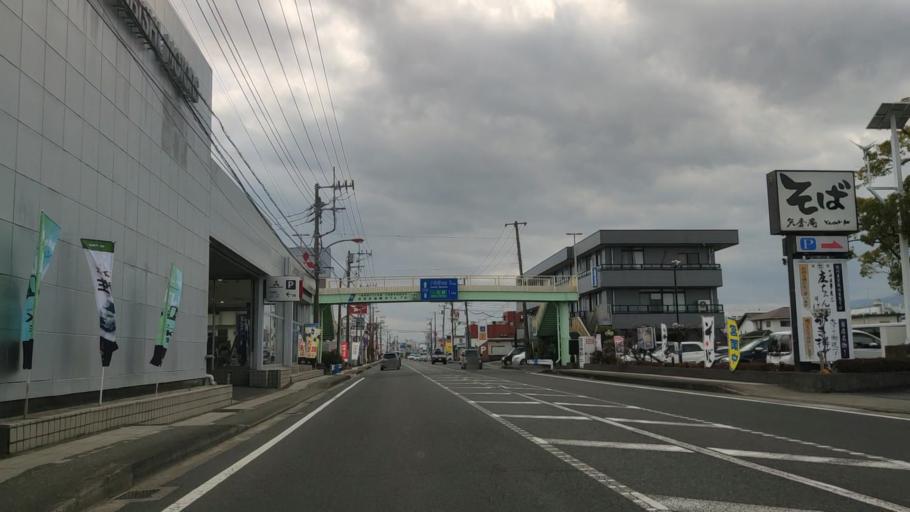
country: JP
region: Kanagawa
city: Odawara
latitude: 35.2963
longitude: 139.1673
